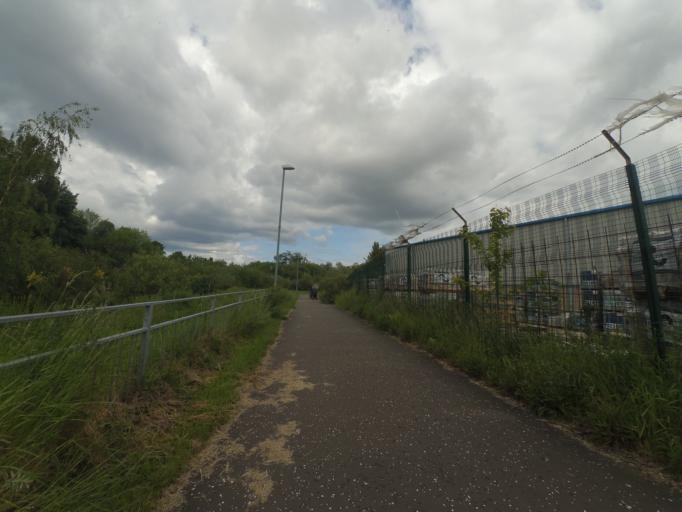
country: GB
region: Scotland
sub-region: West Lothian
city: Seafield
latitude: 55.9359
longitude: -3.1448
